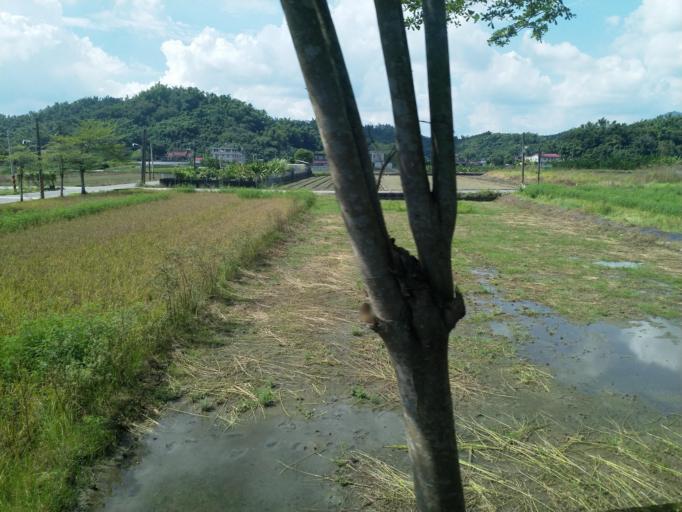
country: TW
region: Taiwan
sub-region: Pingtung
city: Pingtung
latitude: 22.8912
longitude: 120.5797
